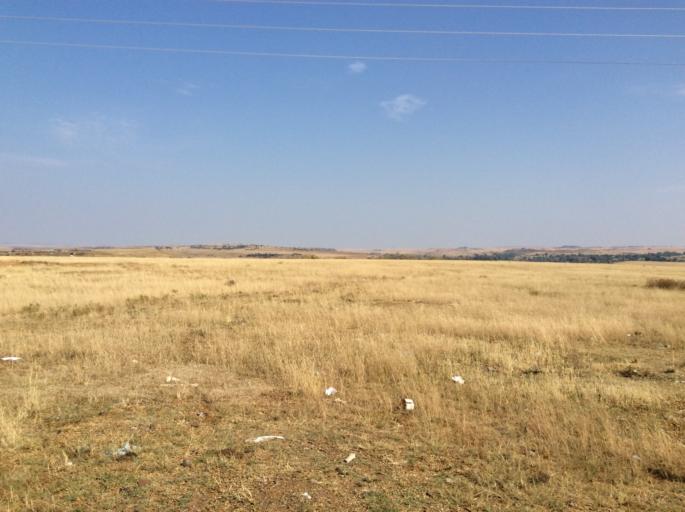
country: LS
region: Mafeteng
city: Mafeteng
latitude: -29.7166
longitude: 27.0107
